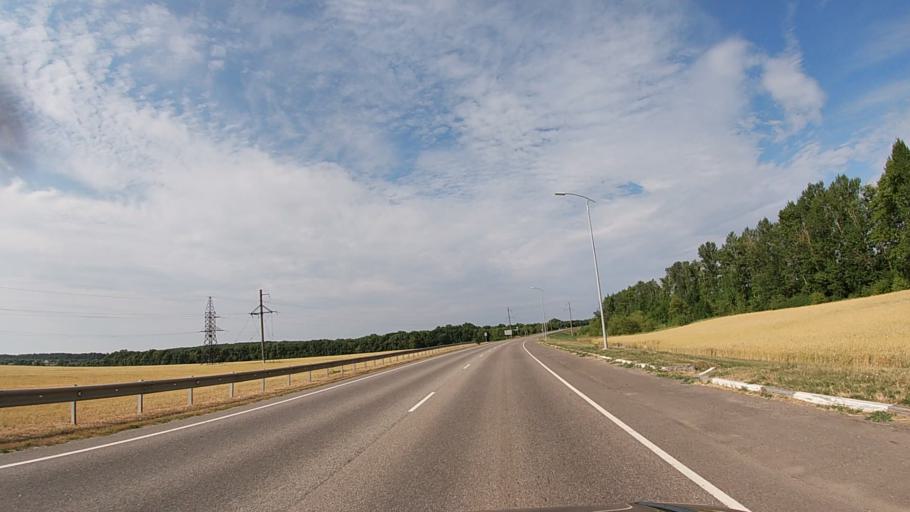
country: RU
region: Belgorod
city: Proletarskiy
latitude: 50.8065
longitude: 35.7428
